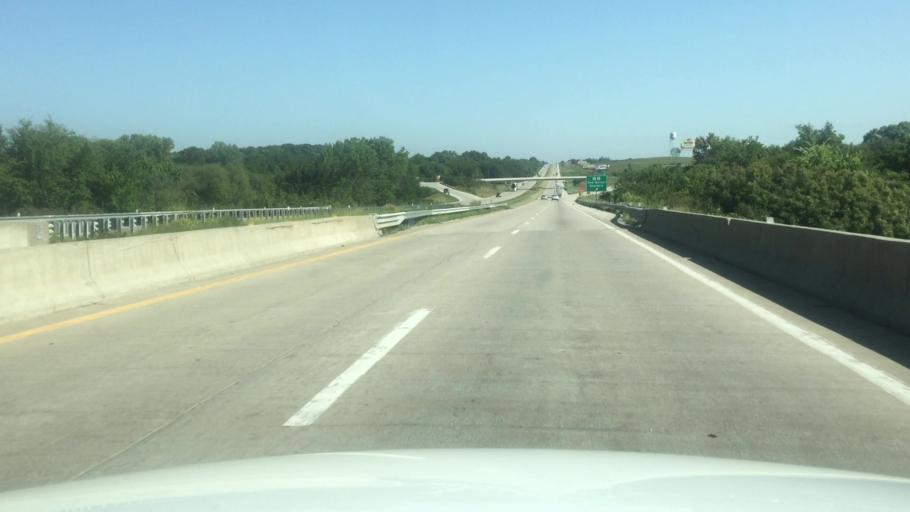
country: US
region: Missouri
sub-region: Platte County
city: Platte City
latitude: 39.5118
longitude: -94.7866
